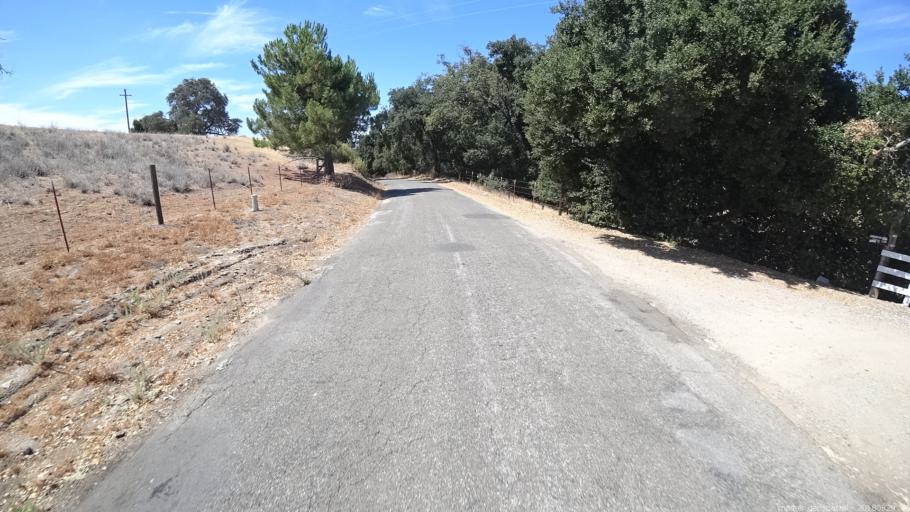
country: US
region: California
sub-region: San Luis Obispo County
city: Lake Nacimiento
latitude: 35.8084
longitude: -121.0476
